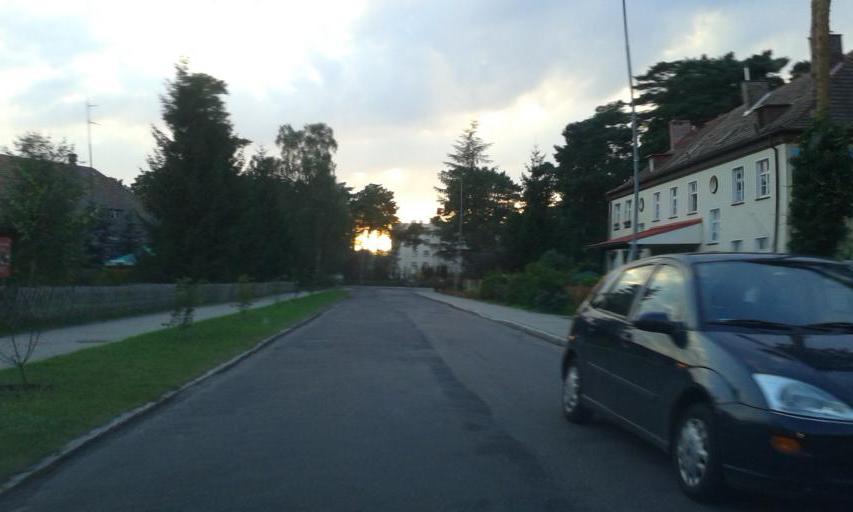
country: PL
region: West Pomeranian Voivodeship
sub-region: Powiat szczecinecki
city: Borne Sulinowo
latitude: 53.5860
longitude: 16.5396
